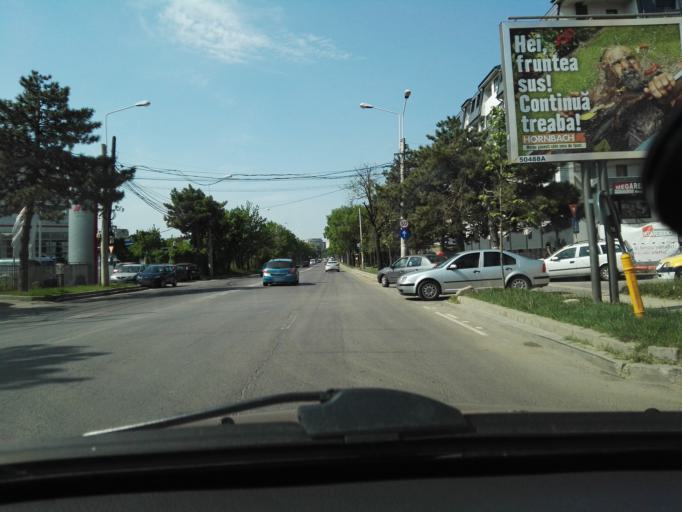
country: RO
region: Ilfov
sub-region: Comuna Popesti-Leordeni
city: Popesti-Leordeni
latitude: 44.3707
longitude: 26.1233
